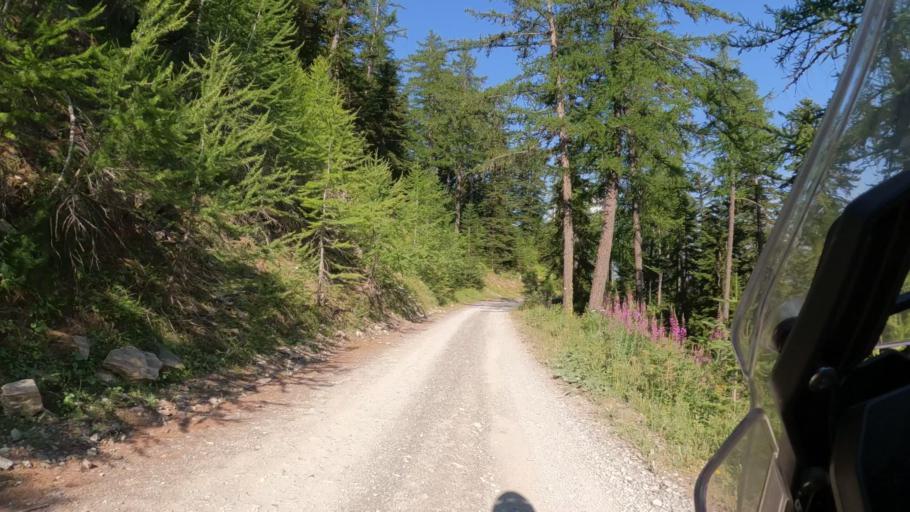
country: FR
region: Provence-Alpes-Cote d'Azur
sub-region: Departement des Hautes-Alpes
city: Embrun
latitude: 44.5912
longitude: 6.5813
